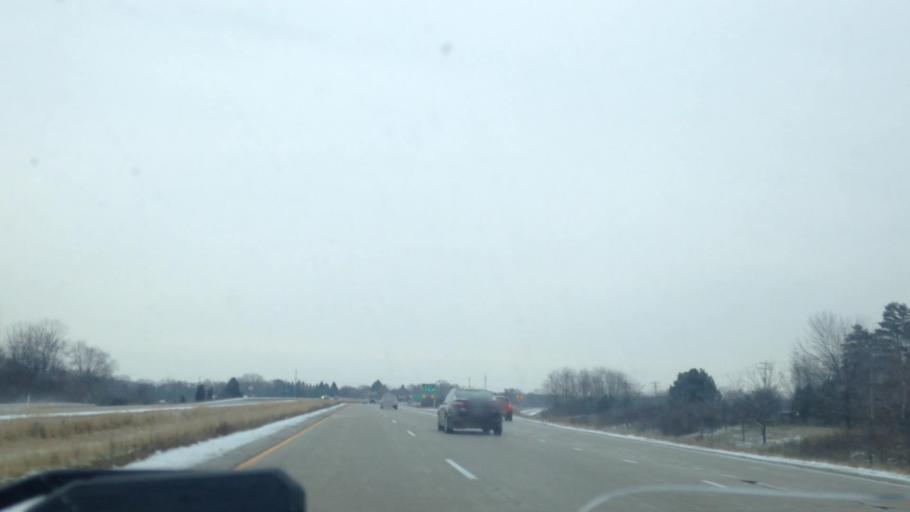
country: US
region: Wisconsin
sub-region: Waukesha County
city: Okauchee Lake
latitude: 43.1082
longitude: -88.4372
